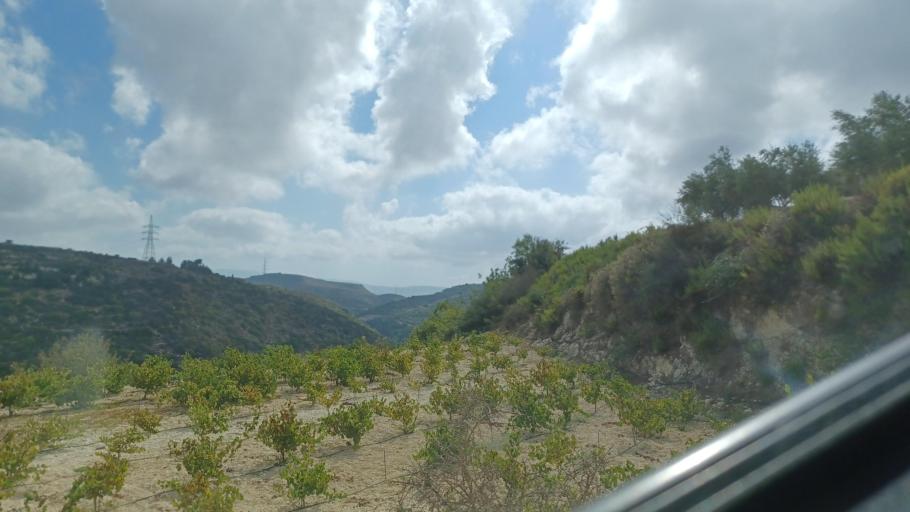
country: CY
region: Pafos
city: Tala
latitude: 34.8706
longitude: 32.4570
